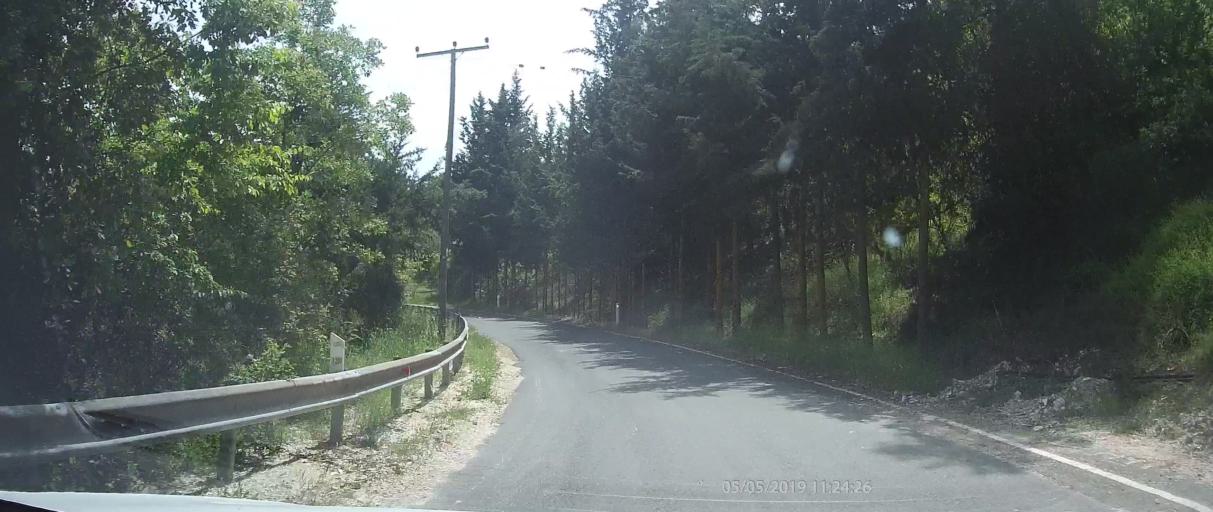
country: CY
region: Limassol
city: Pachna
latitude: 34.9216
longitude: 32.6395
